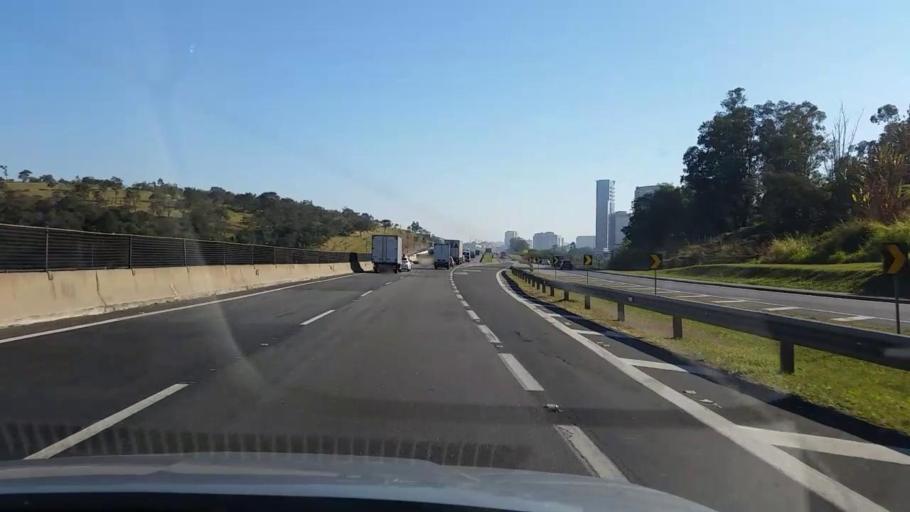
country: BR
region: Sao Paulo
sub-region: Jundiai
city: Jundiai
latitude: -23.2026
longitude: -46.9016
